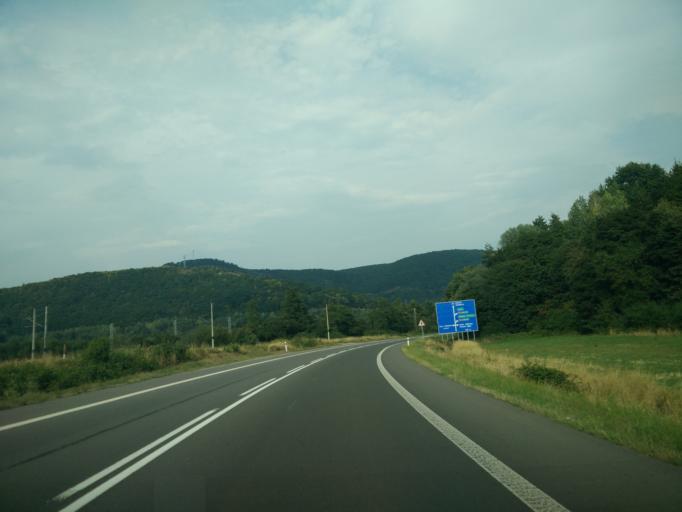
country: SK
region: Banskobystricky
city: Ziar nad Hronom
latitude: 48.5867
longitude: 18.8823
